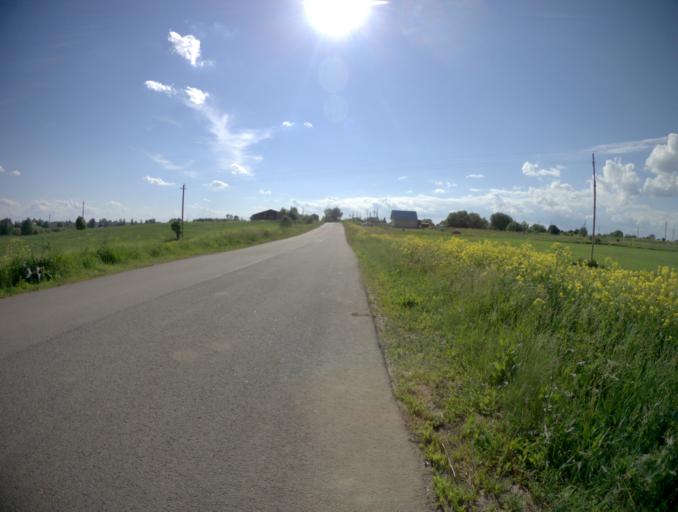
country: RU
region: Vladimir
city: Suzdal'
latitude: 56.3393
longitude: 40.4512
